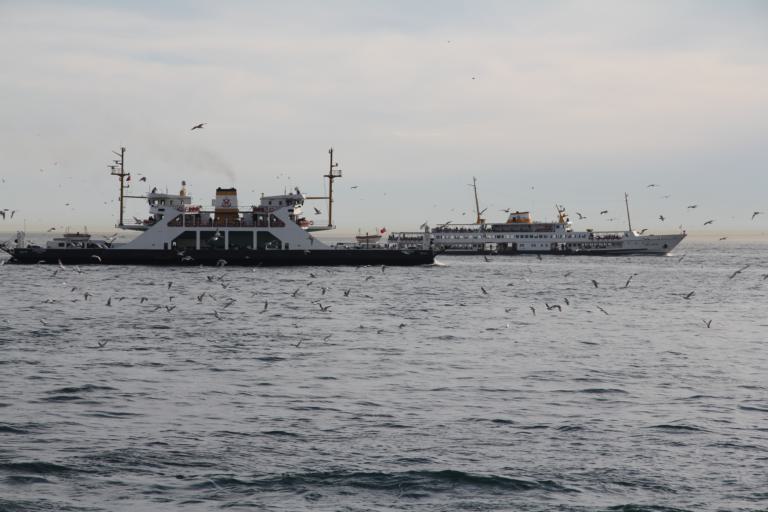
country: TR
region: Istanbul
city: Eminoenue
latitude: 41.0211
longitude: 28.9936
